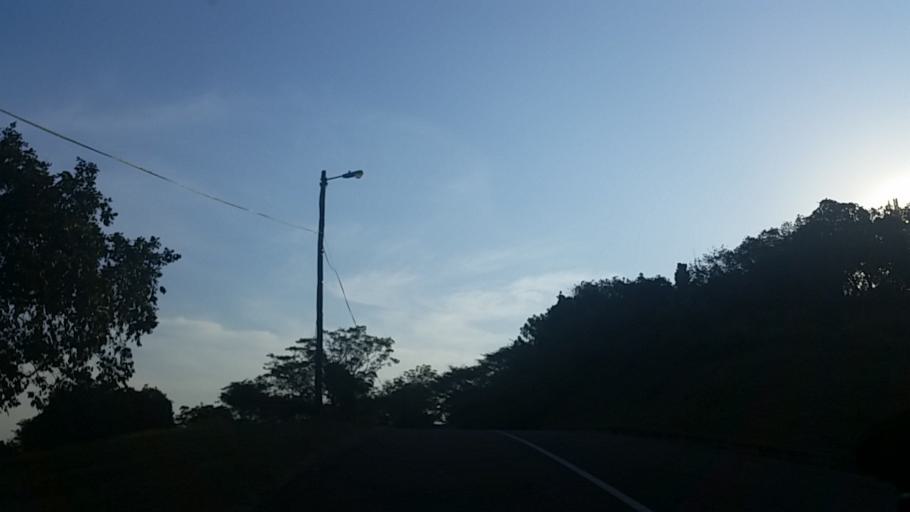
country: ZA
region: KwaZulu-Natal
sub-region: eThekwini Metropolitan Municipality
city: Berea
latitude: -29.8494
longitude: 30.9218
